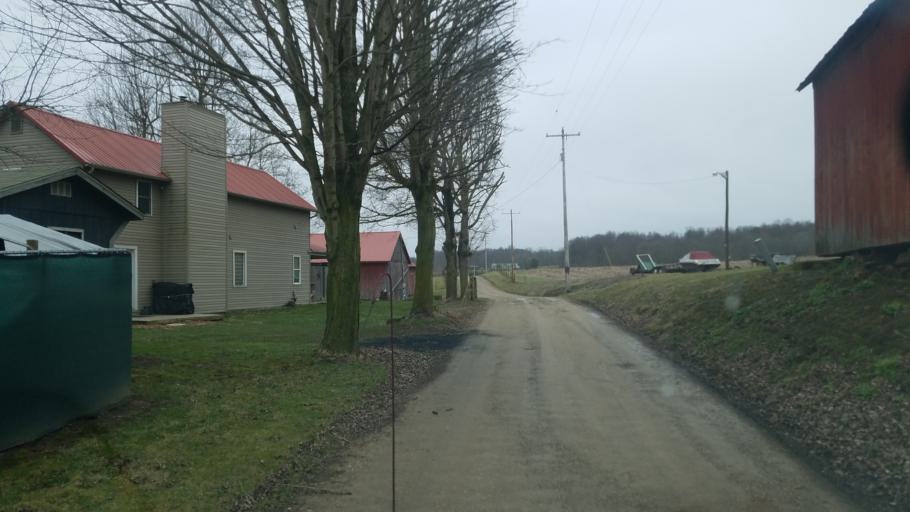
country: US
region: Ohio
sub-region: Knox County
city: Gambier
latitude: 40.4636
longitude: -82.4092
